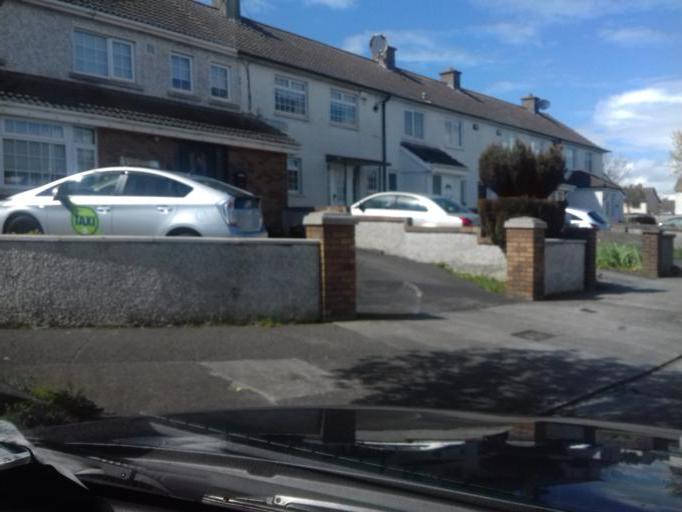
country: IE
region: Leinster
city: Donaghmede
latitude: 53.3891
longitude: -6.1655
